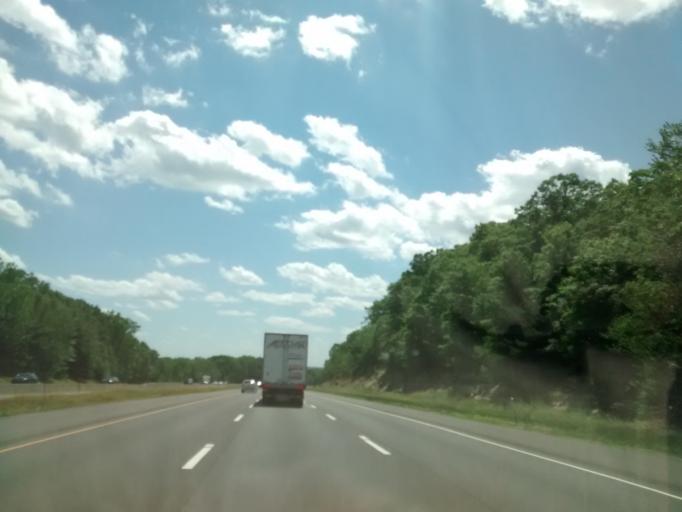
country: US
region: Connecticut
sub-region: Tolland County
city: Rockville
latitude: 41.8469
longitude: -72.4411
